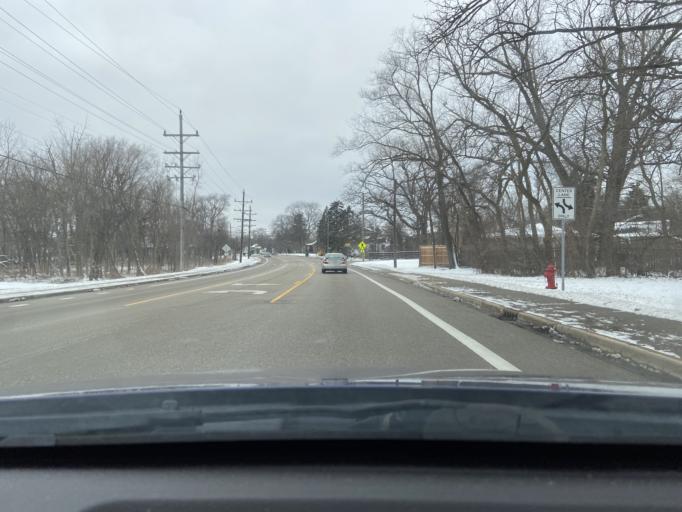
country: US
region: Illinois
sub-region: Lake County
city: Round Lake Park
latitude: 42.3596
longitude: -88.0856
